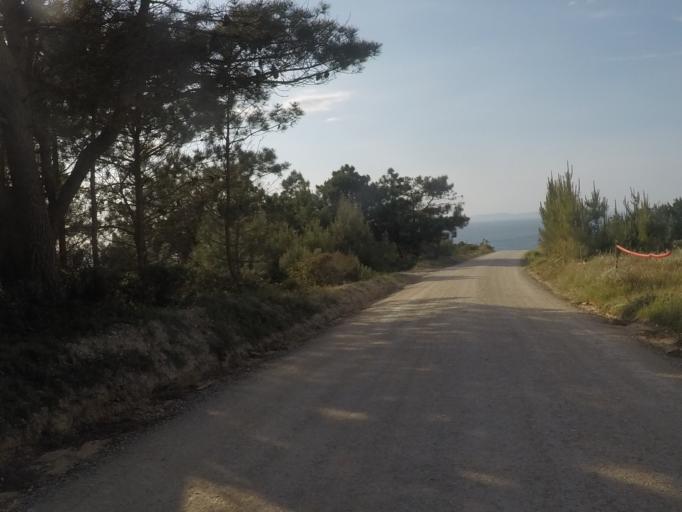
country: PT
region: Setubal
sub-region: Sesimbra
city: Sesimbra
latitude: 38.4479
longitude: -9.1996
